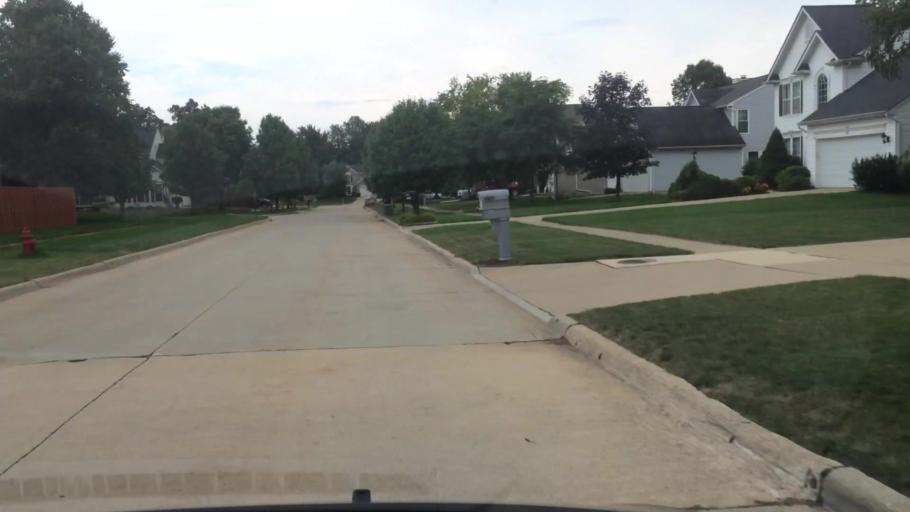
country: US
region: Ohio
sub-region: Medina County
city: Brunswick
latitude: 41.2726
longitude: -81.8174
